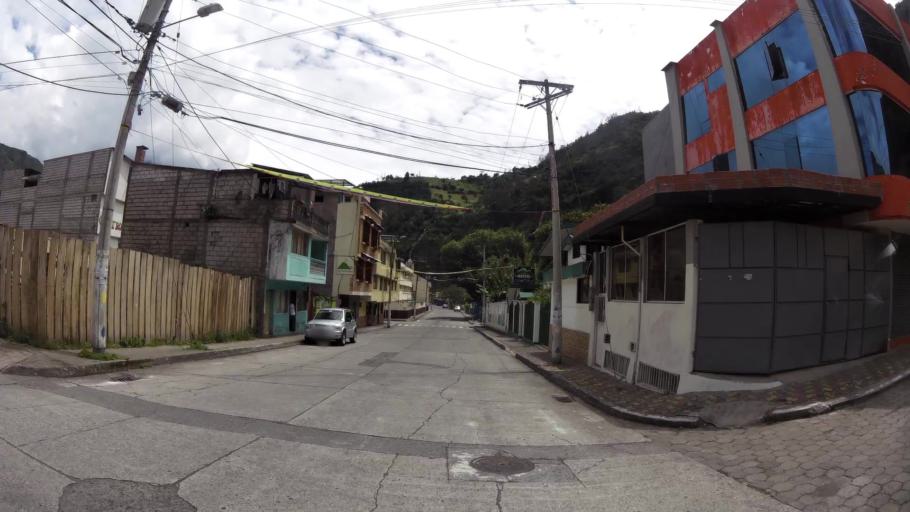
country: EC
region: Tungurahua
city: Banos
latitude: -1.3999
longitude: -78.4242
